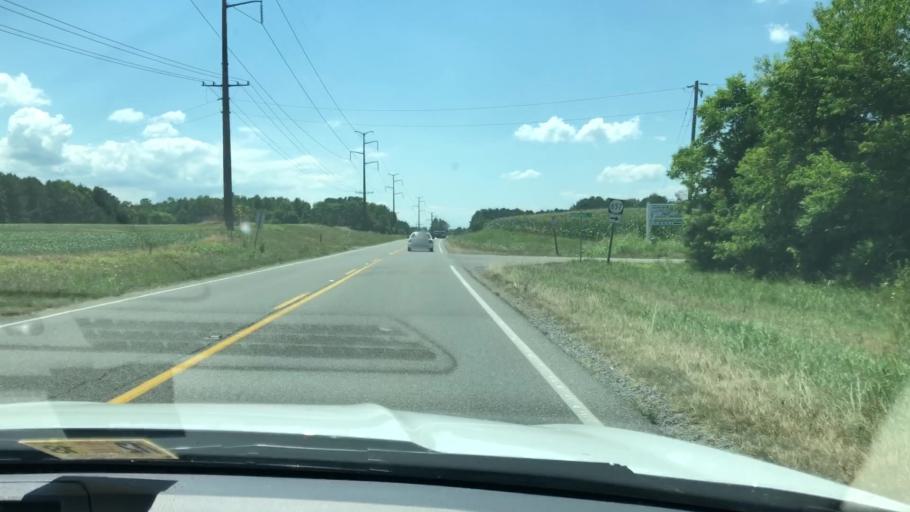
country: US
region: Virginia
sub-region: Middlesex County
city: Saluda
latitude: 37.5862
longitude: -76.4779
